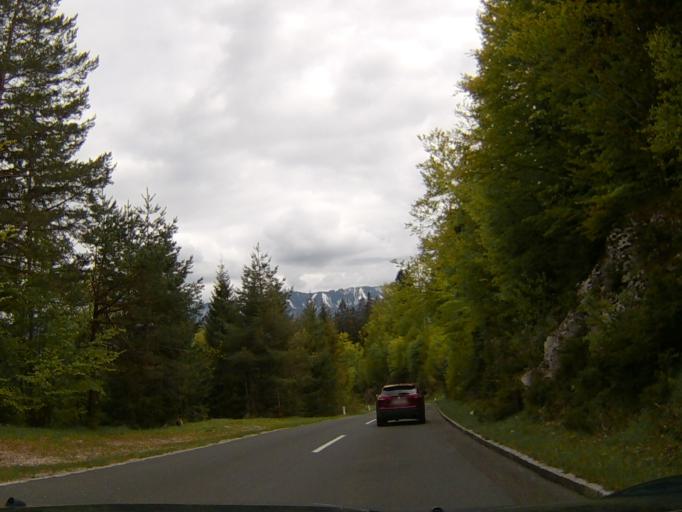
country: AT
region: Carinthia
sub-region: Politischer Bezirk Villach Land
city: Arnoldstein
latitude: 46.5847
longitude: 13.7792
